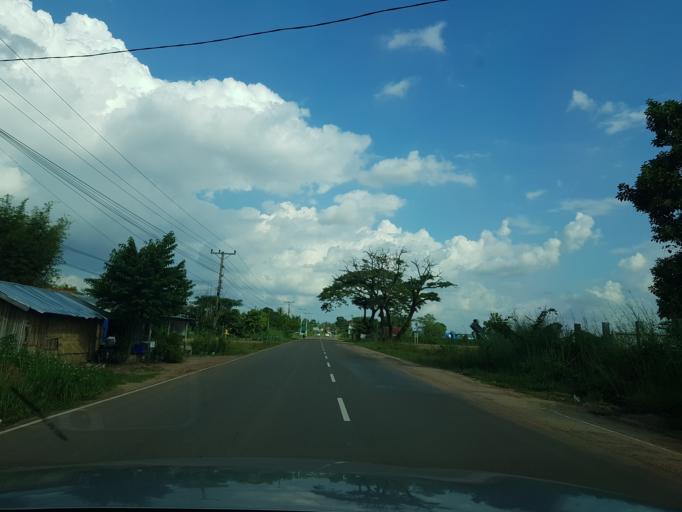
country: TH
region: Nong Khai
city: Pho Tak
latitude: 17.9807
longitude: 102.4572
